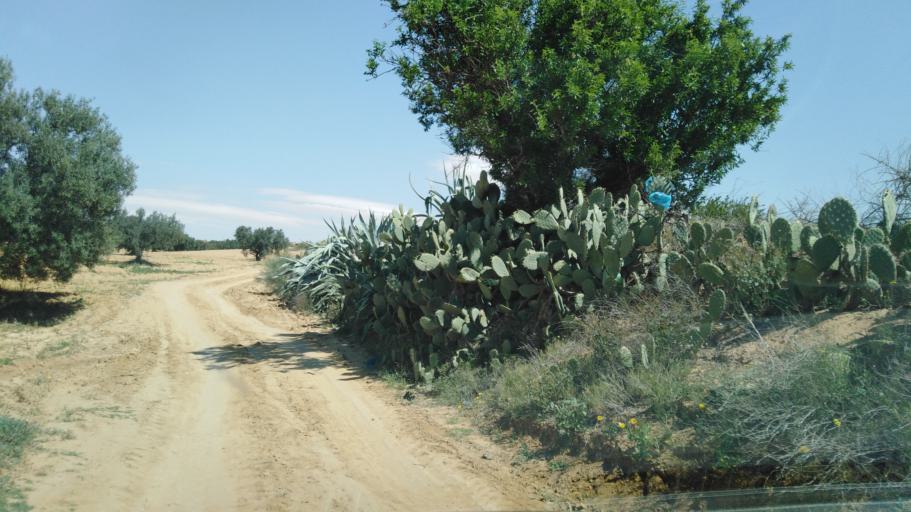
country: TN
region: Safaqis
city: Sfax
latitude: 34.7810
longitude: 10.5282
